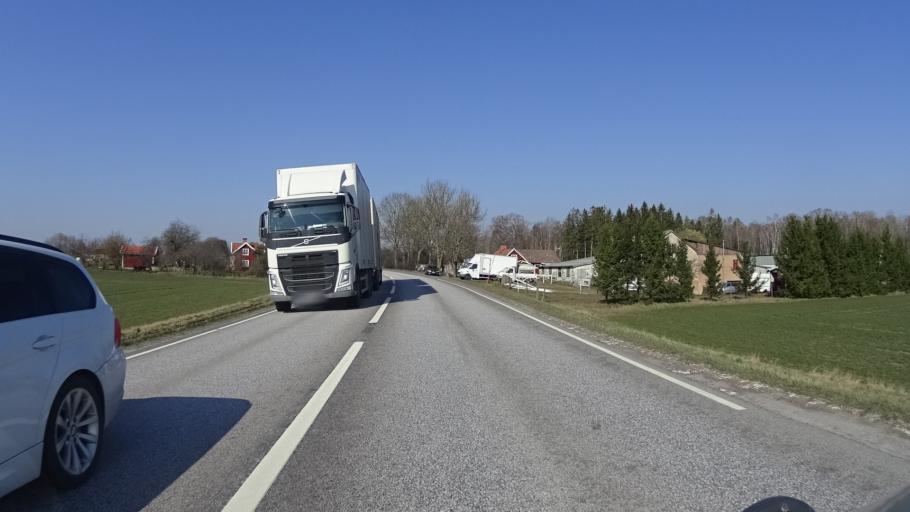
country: SE
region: OEstergoetland
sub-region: Mjolby Kommun
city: Mantorp
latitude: 58.3776
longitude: 15.2602
